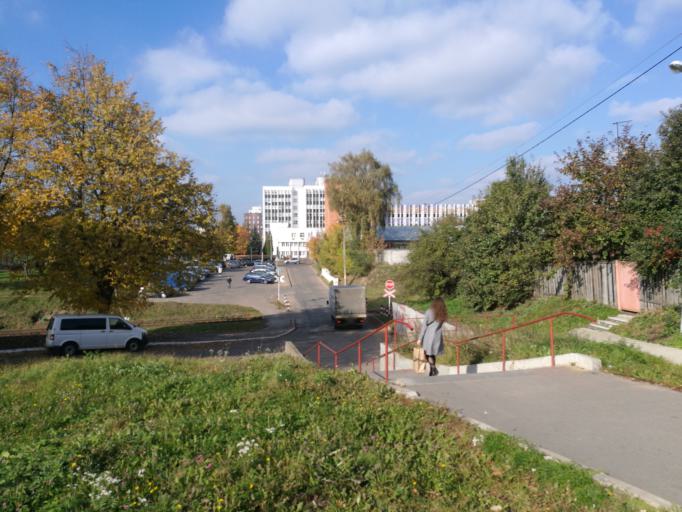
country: BY
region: Minsk
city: Minsk
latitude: 53.8995
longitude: 27.5171
